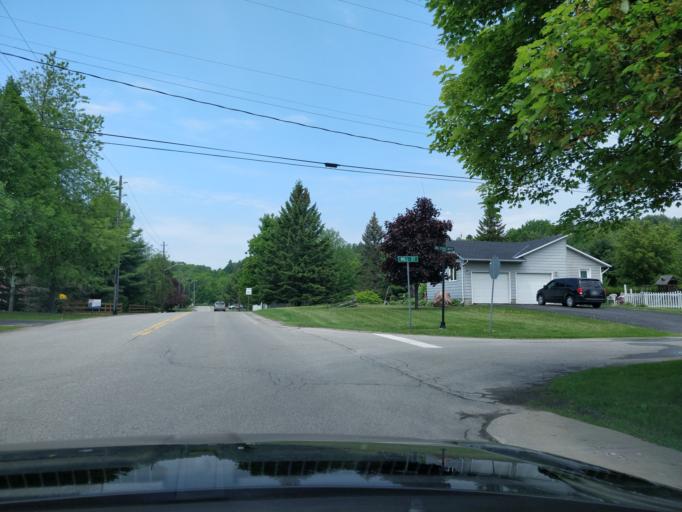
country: CA
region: Ontario
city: Perth
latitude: 44.6813
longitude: -76.4067
